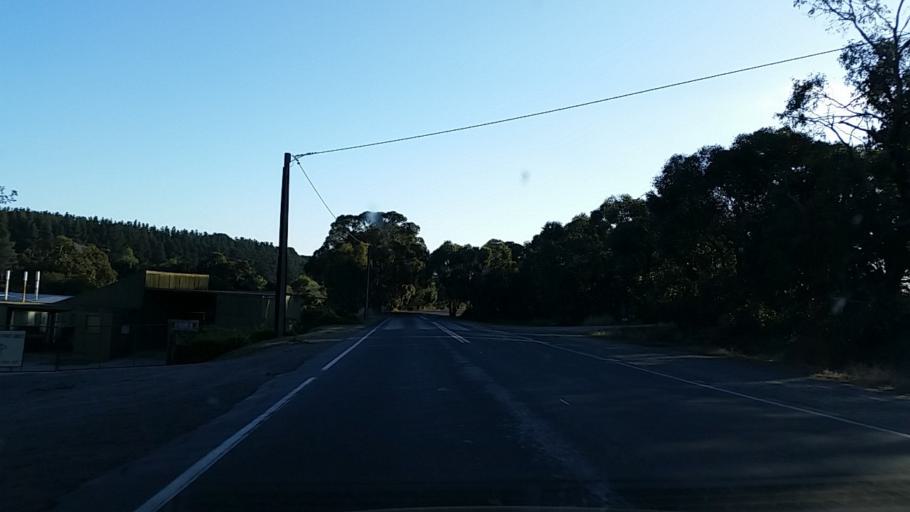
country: AU
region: South Australia
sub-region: Alexandrina
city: Mount Compass
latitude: -35.3491
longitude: 138.6365
